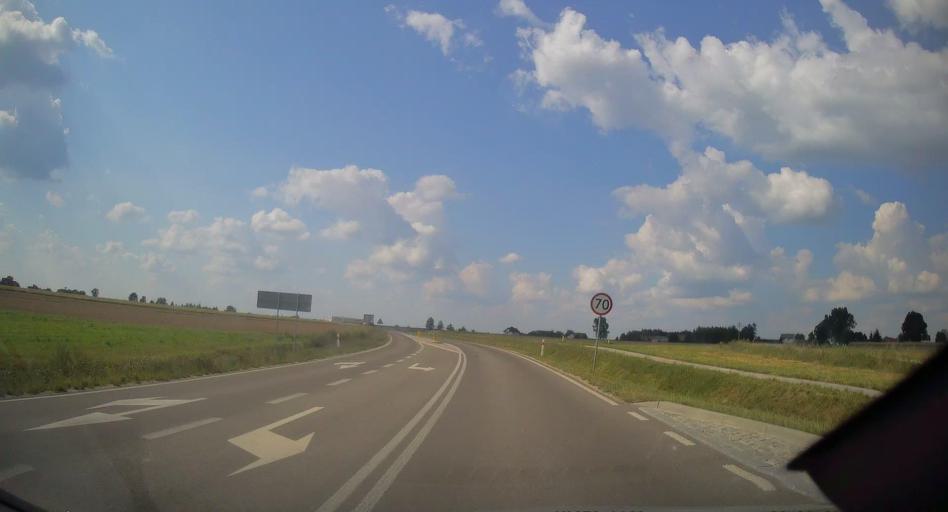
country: PL
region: Swietokrzyskie
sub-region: Powiat kielecki
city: Lopuszno
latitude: 50.9720
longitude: 20.2497
